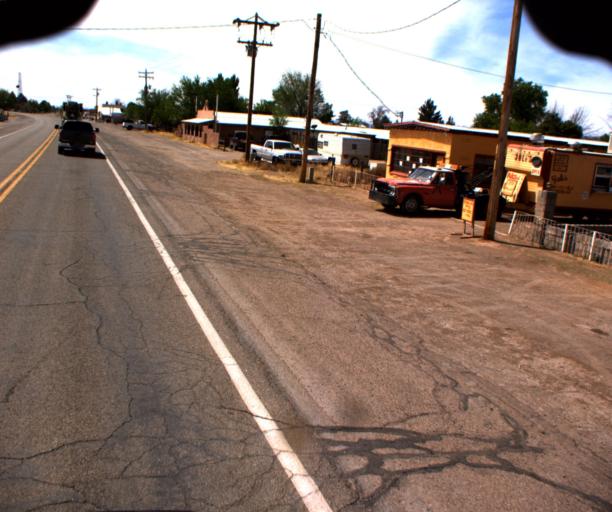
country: US
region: Arizona
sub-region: Cochise County
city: Bisbee
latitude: 31.6845
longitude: -109.6874
